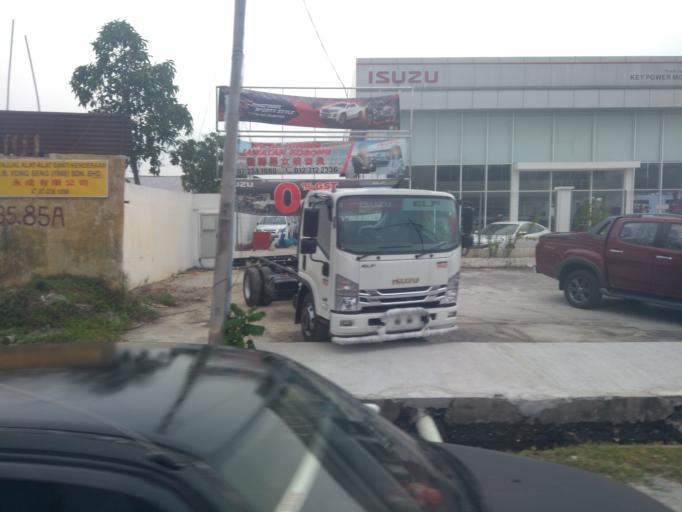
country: MY
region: Johor
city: Johor Bahru
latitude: 1.4875
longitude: 103.7143
